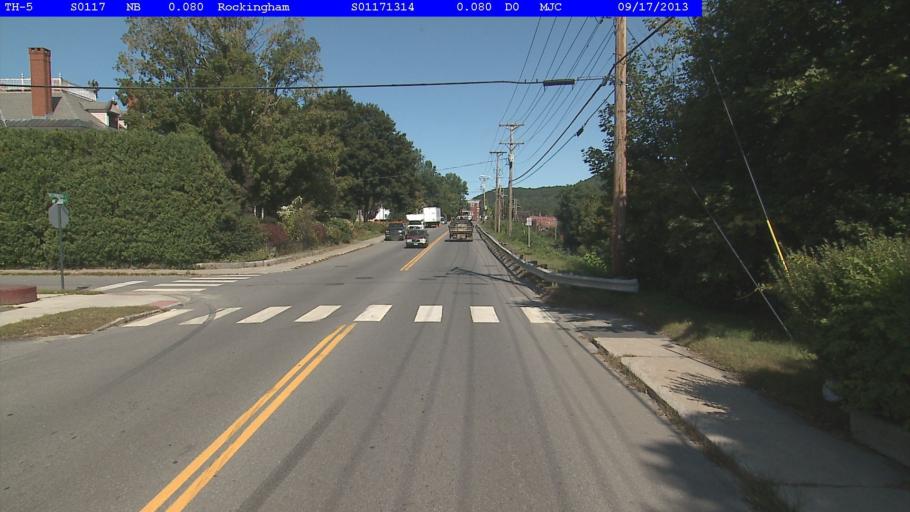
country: US
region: Vermont
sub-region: Windham County
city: Bellows Falls
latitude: 43.1297
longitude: -72.4443
